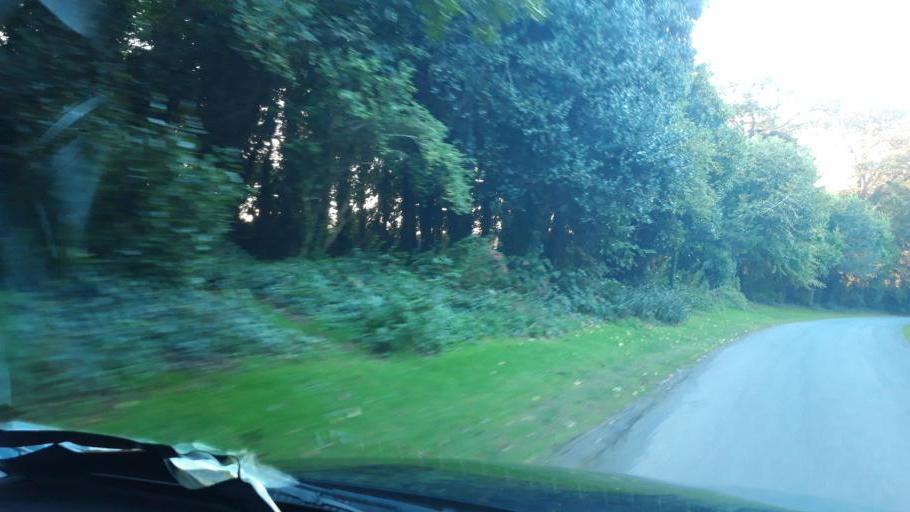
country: IE
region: Leinster
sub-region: Fingal County
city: Howth
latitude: 53.3872
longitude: -6.0797
